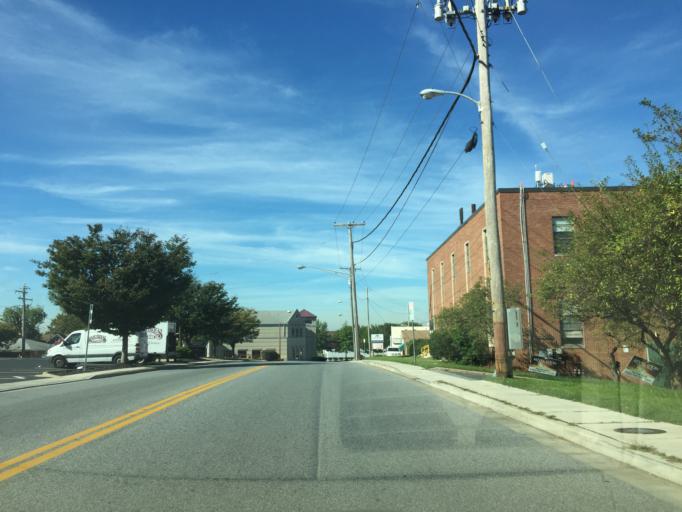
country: US
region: Maryland
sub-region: Baltimore County
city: Dundalk
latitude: 39.2723
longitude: -76.5277
